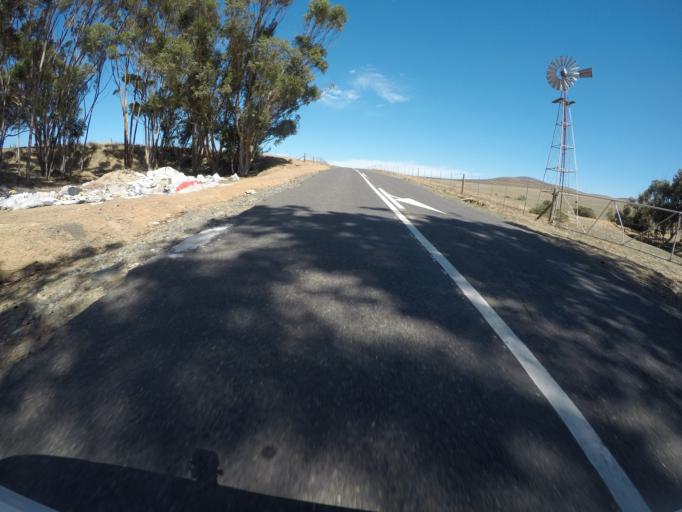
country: ZA
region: Western Cape
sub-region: City of Cape Town
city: Atlantis
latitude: -33.7002
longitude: 18.5884
